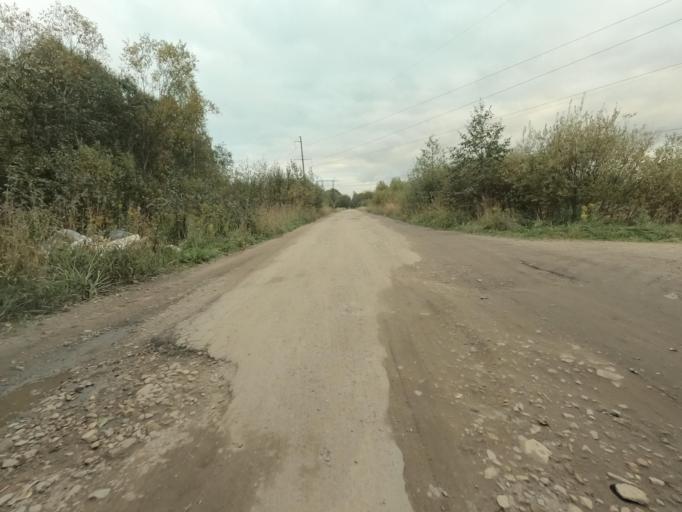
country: RU
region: St.-Petersburg
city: Sapernyy
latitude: 59.7598
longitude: 30.6558
